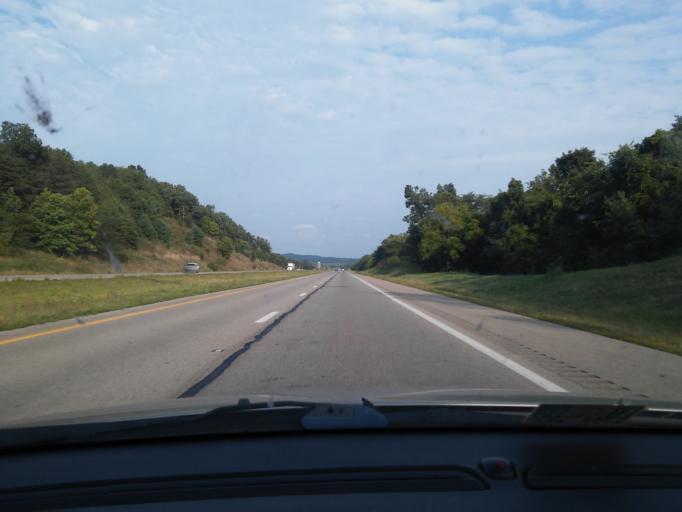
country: US
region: Ohio
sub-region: Gallia County
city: Gallipolis
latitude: 38.8667
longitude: -82.2685
